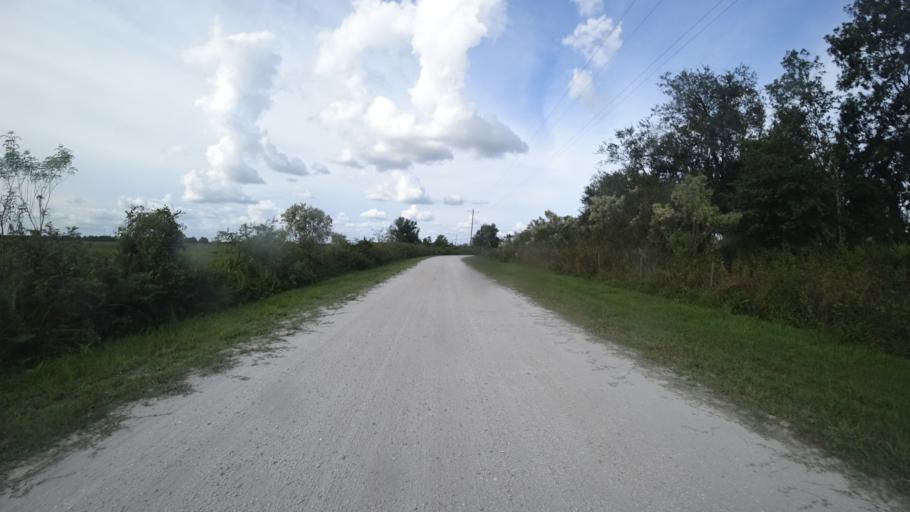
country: US
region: Florida
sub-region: DeSoto County
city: Arcadia
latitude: 27.2919
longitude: -82.1053
